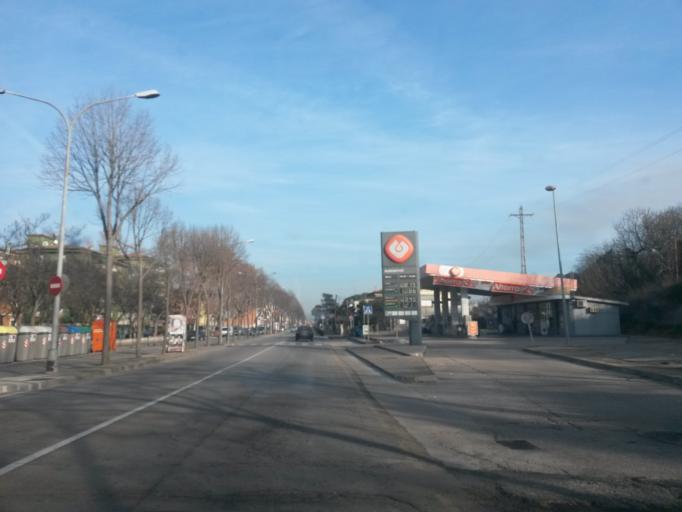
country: ES
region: Catalonia
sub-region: Provincia de Girona
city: Sarria de Ter
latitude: 42.0036
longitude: 2.8247
